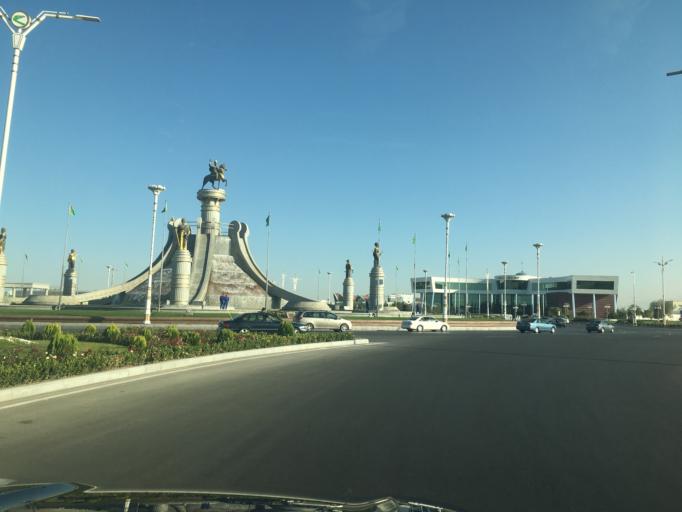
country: TM
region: Ahal
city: Ashgabat
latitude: 37.9742
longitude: 58.3891
